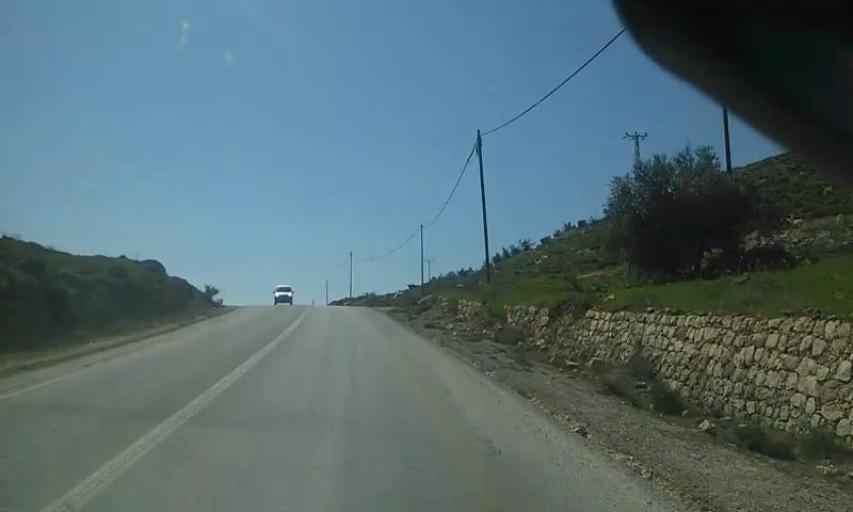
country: PS
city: Khursa
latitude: 31.4766
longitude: 35.0437
